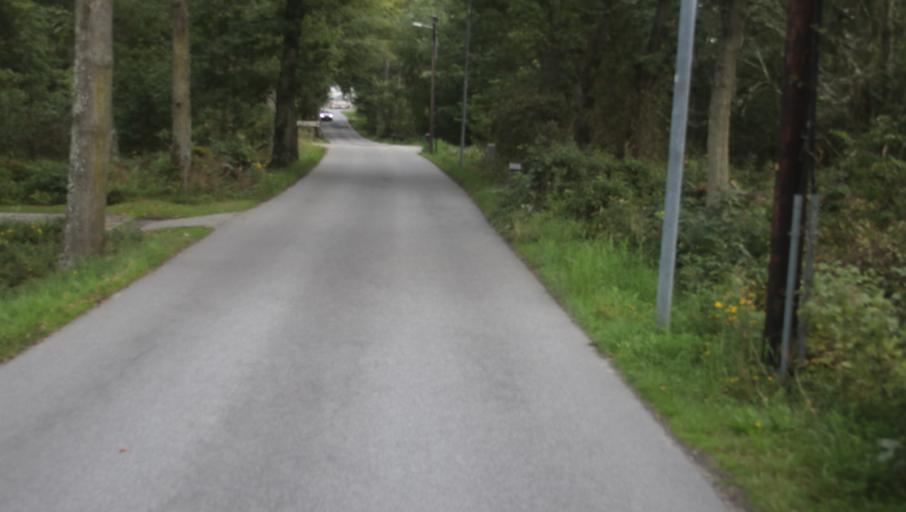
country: SE
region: Blekinge
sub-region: Karlshamns Kommun
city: Karlshamn
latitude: 56.1580
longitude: 14.8800
